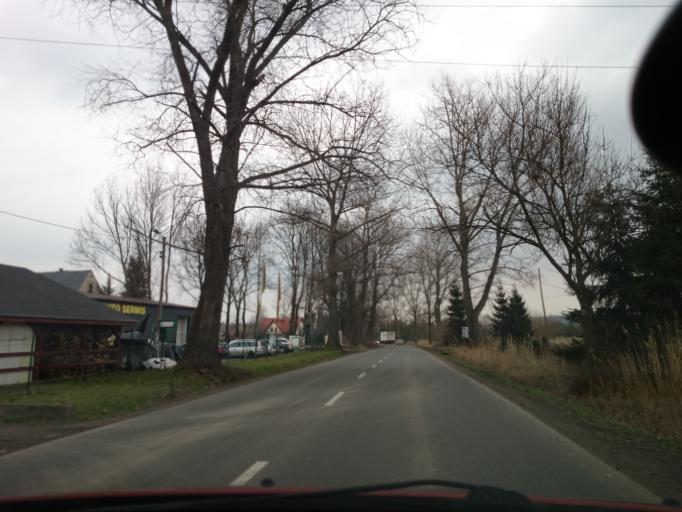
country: PL
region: Lower Silesian Voivodeship
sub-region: Powiat klodzki
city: Polanica-Zdroj
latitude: 50.4258
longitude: 16.5442
